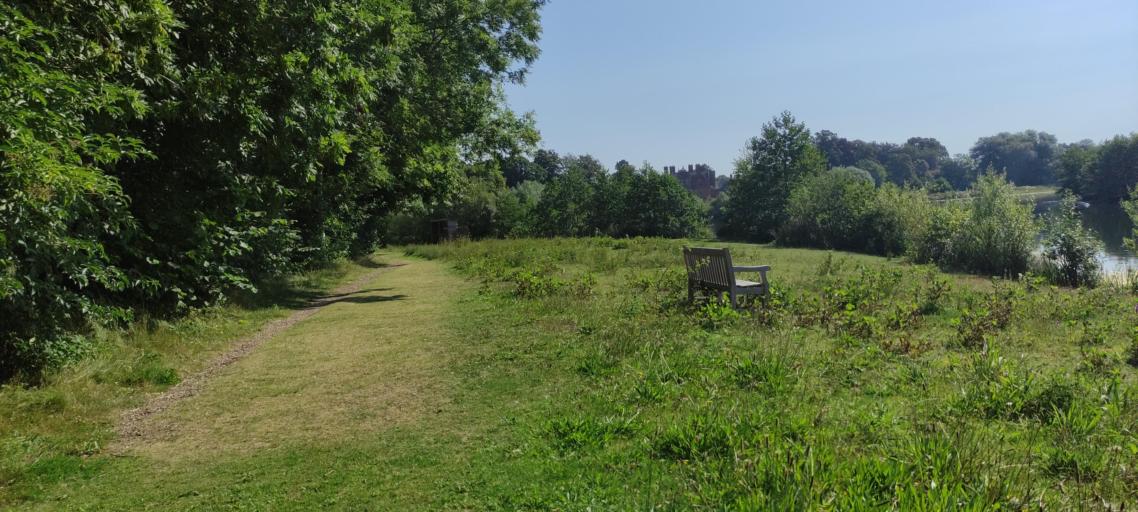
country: GB
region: England
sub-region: North Yorkshire
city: Catterick
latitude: 54.3719
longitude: -1.5844
